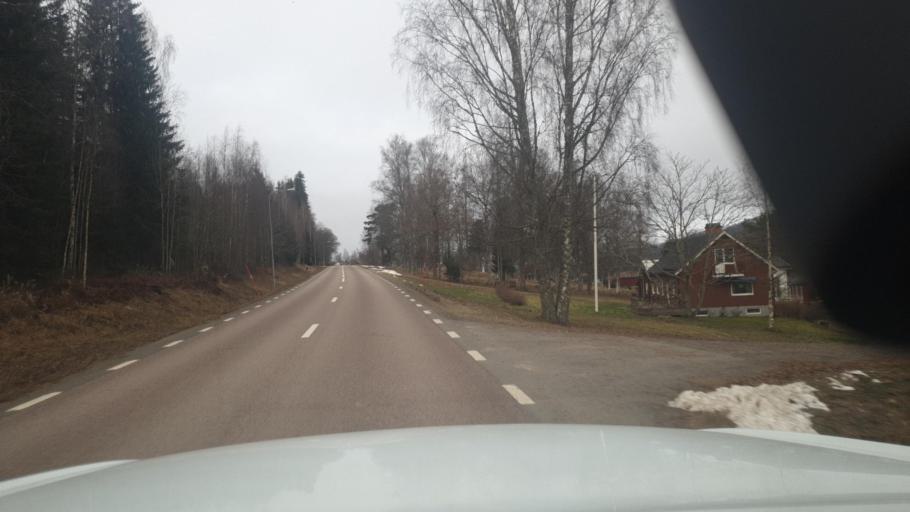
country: SE
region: Vaermland
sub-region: Sunne Kommun
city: Sunne
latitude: 59.8677
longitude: 12.9436
